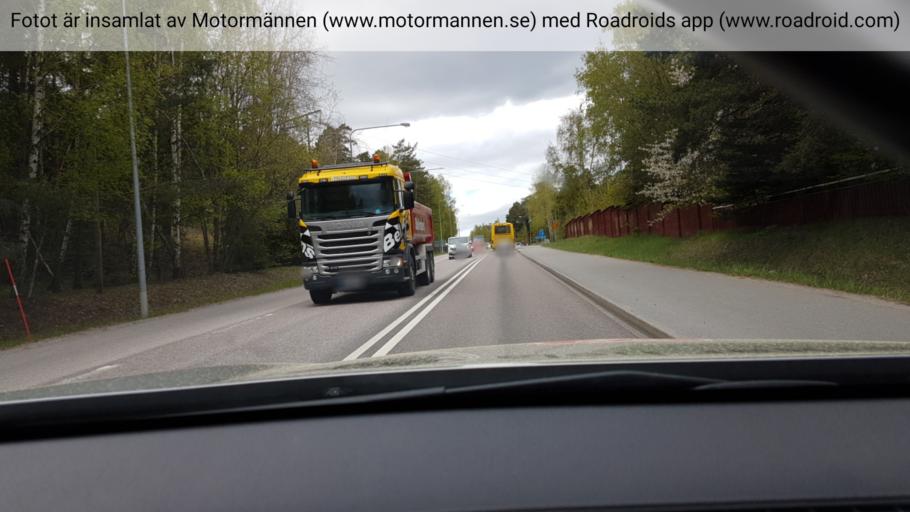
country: SE
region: Stockholm
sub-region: Tyreso Kommun
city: Bollmora
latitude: 59.2313
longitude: 18.1955
